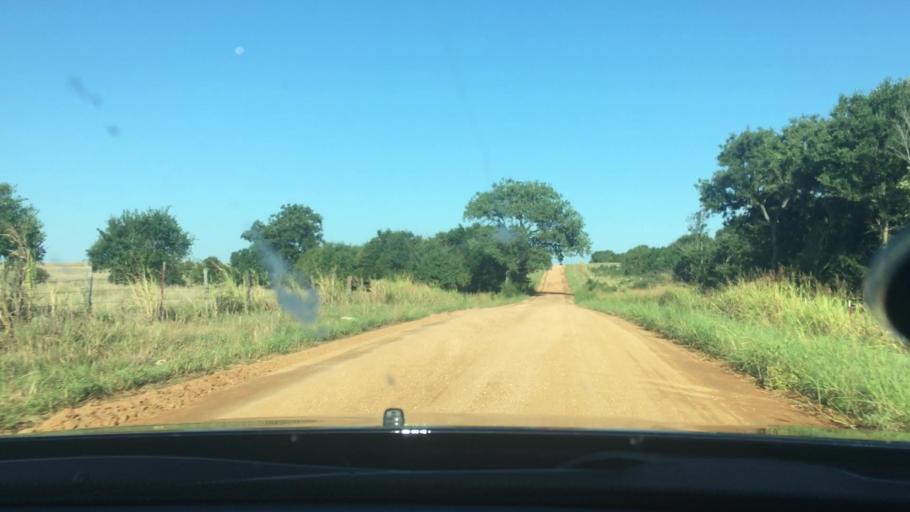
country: US
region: Oklahoma
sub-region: Murray County
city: Sulphur
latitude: 34.4195
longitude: -96.7799
